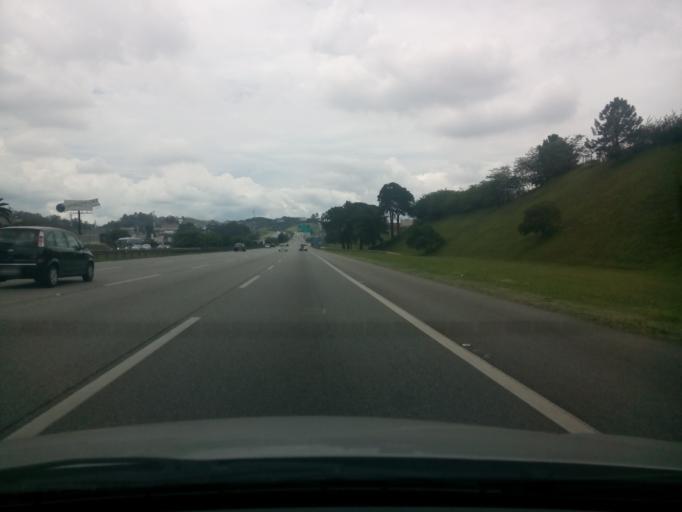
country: BR
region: Sao Paulo
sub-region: Diadema
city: Diadema
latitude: -23.7136
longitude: -46.6048
